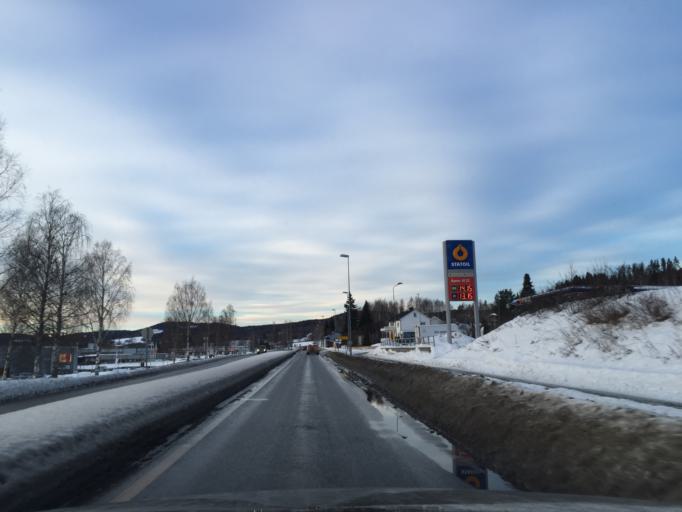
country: NO
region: Hedmark
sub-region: Kongsvinger
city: Kongsvinger
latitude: 60.2023
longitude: 11.9779
